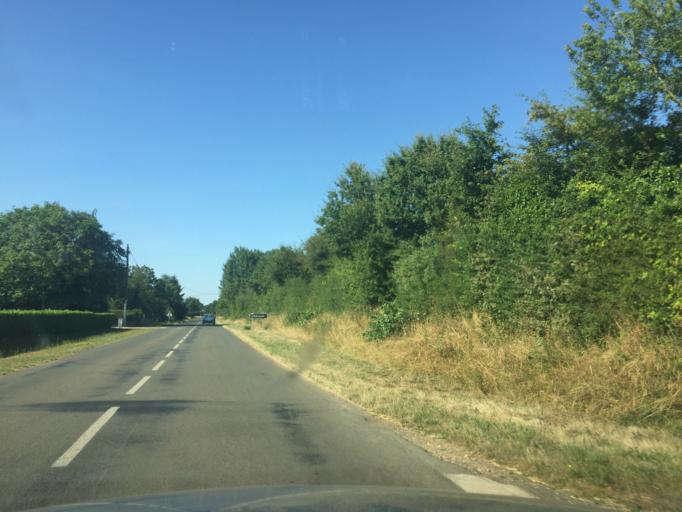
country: FR
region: Poitou-Charentes
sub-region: Departement des Deux-Sevres
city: Lezay
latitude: 46.1982
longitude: -0.0379
